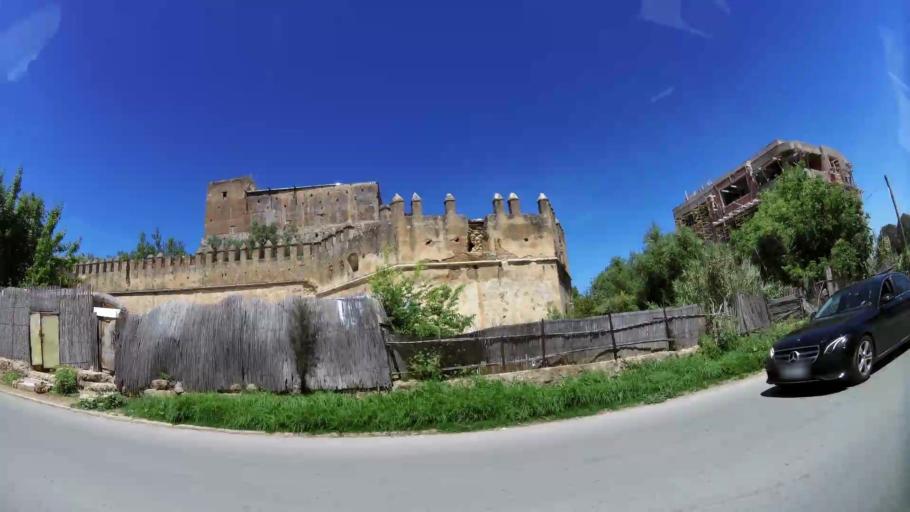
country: MA
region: Fes-Boulemane
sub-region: Fes
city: Fes
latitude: 34.0266
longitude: -5.0008
